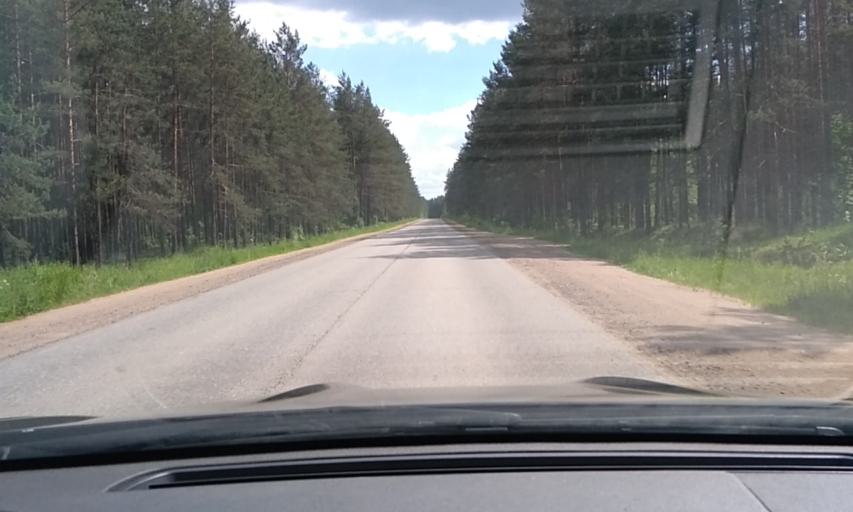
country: RU
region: Leningrad
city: Imeni Sverdlova
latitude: 59.8481
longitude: 30.6834
